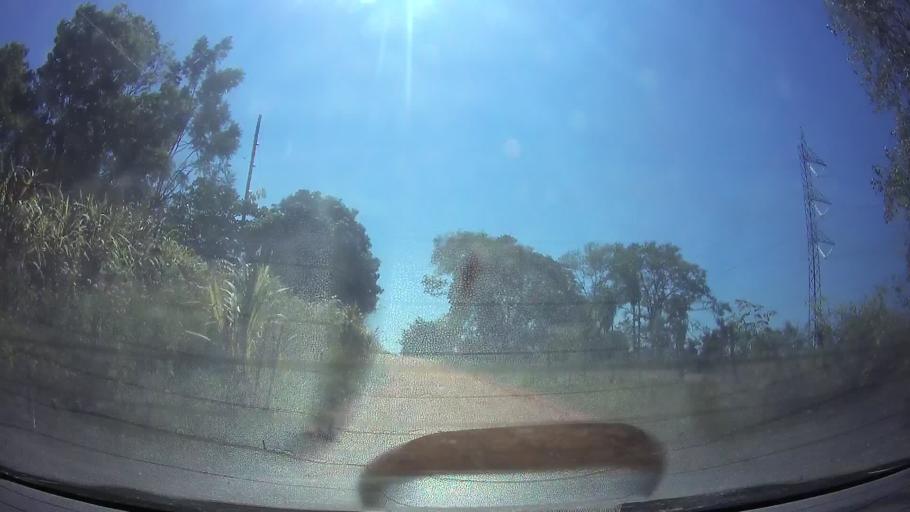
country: PY
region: Central
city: Limpio
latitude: -25.2411
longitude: -57.4433
